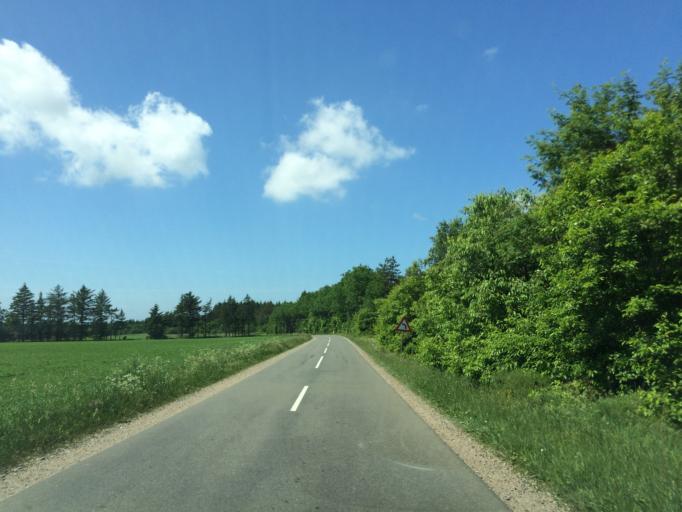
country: DK
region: Central Jutland
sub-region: Holstebro Kommune
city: Ulfborg
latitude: 56.2053
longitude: 8.4695
